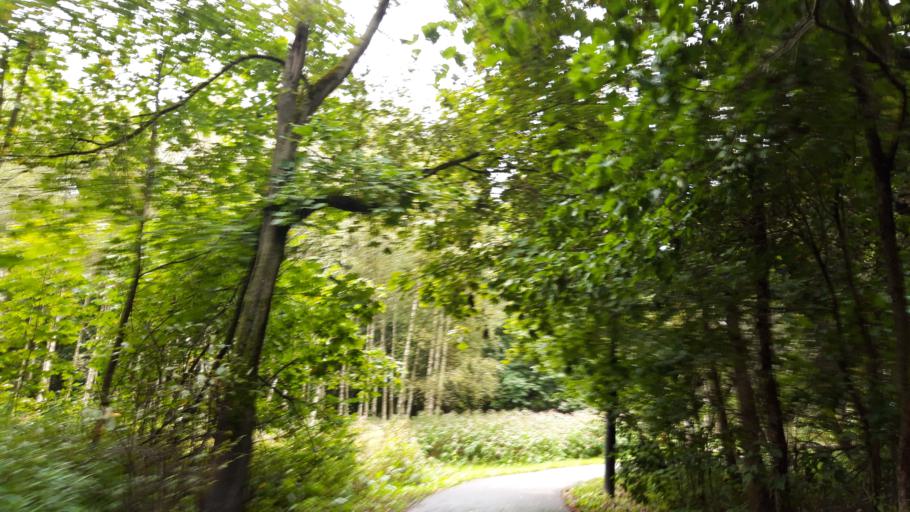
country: RU
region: Moscow
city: Zelenograd
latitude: 55.9911
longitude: 37.1967
